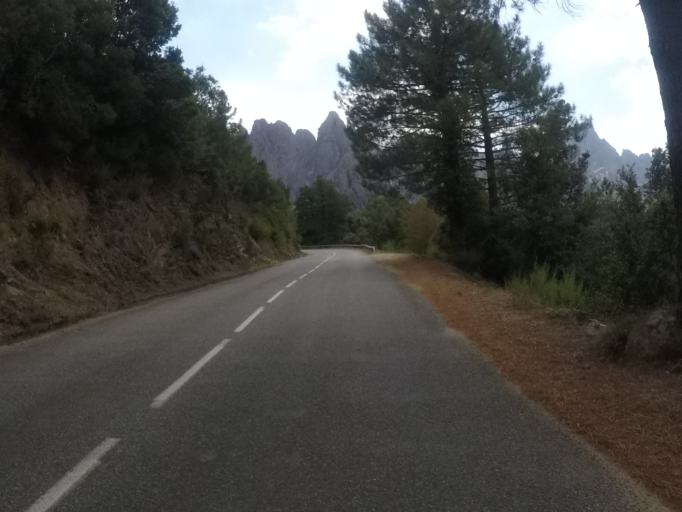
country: FR
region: Corsica
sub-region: Departement de la Corse-du-Sud
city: Sari-Solenzara
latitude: 41.8282
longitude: 9.2716
